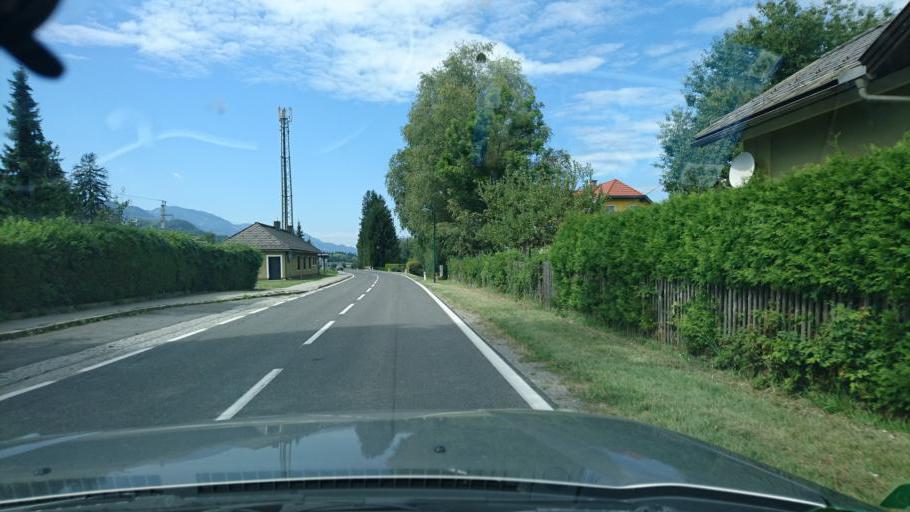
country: AT
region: Carinthia
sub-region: Politischer Bezirk Villach Land
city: Finkenstein am Faaker See
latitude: 46.5647
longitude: 13.9126
